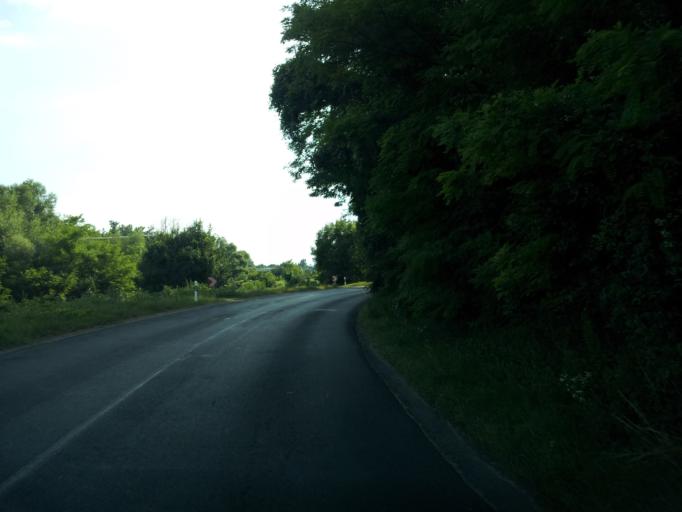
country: HU
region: Veszprem
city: Revfueloep
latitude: 46.9322
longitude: 17.5696
